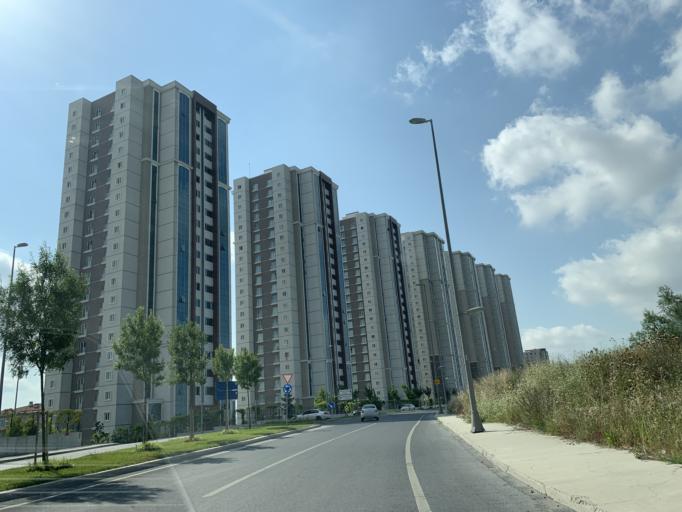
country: TR
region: Istanbul
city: Esenyurt
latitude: 41.0767
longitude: 28.6977
